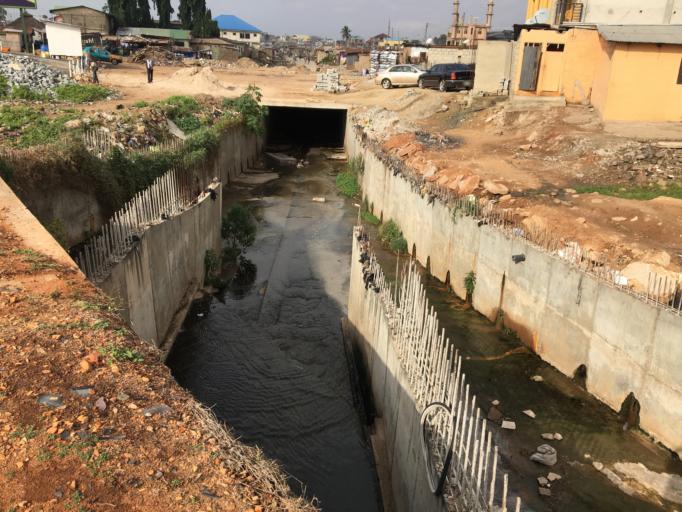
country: GH
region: Greater Accra
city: Accra
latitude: 5.5923
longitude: -0.1898
